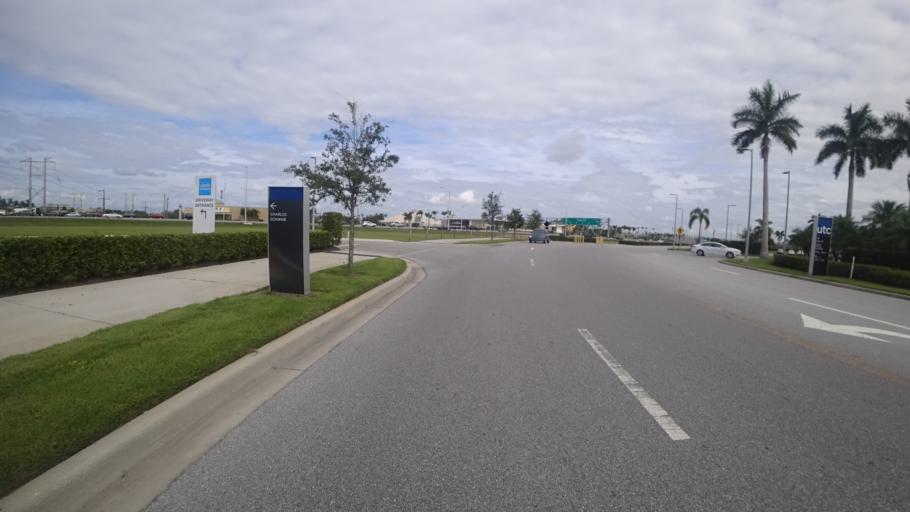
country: US
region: Florida
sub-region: Sarasota County
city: The Meadows
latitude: 27.3876
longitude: -82.4542
